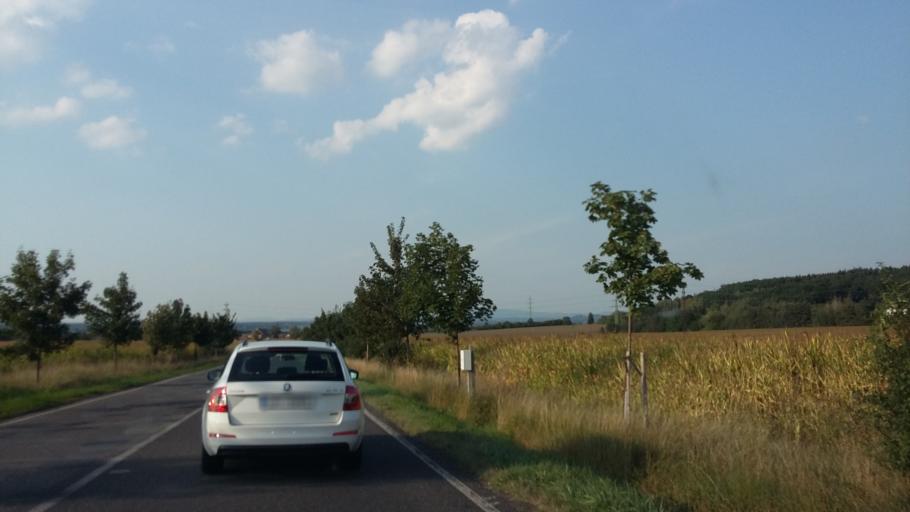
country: CZ
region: Central Bohemia
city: Kosmonosy
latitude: 50.4507
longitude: 14.9314
